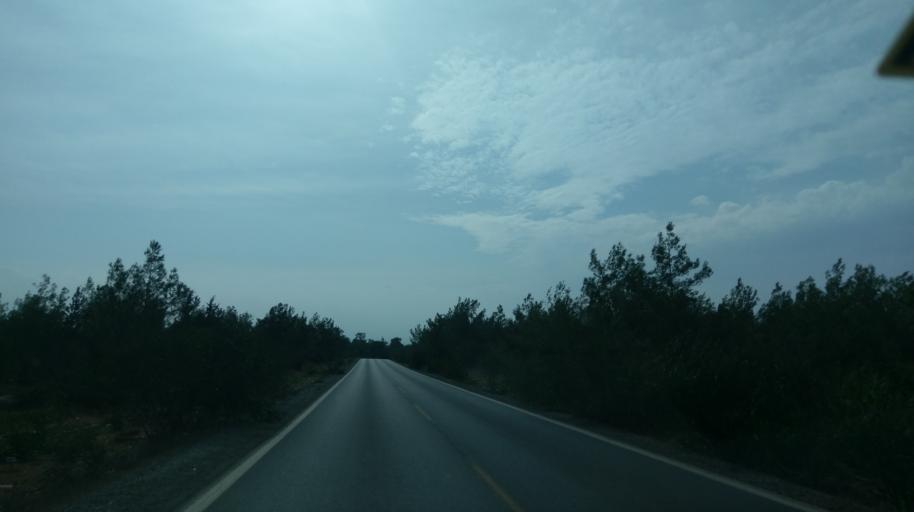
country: CY
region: Lefkosia
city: Morfou
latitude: 35.2836
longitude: 33.0408
